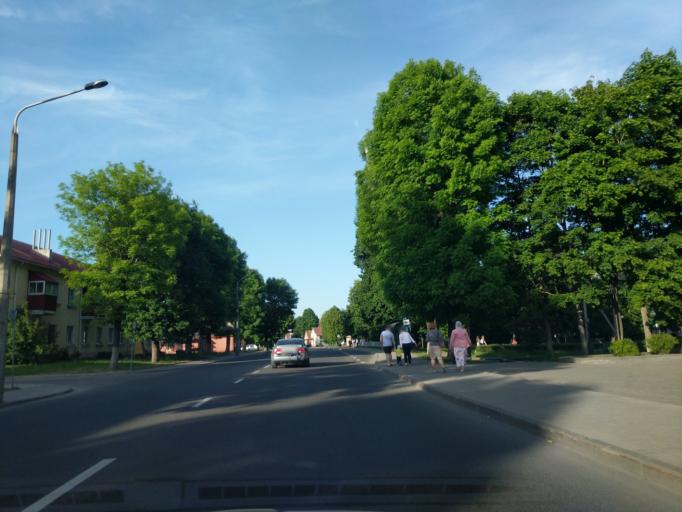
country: BY
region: Grodnenskaya
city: Ashmyany
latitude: 54.4266
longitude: 25.9392
